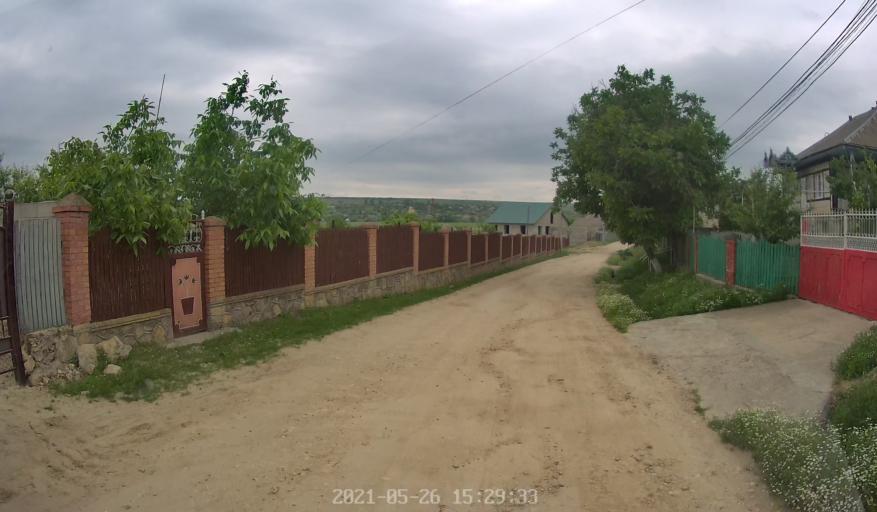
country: MD
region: Hincesti
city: Dancu
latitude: 46.6680
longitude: 28.3201
